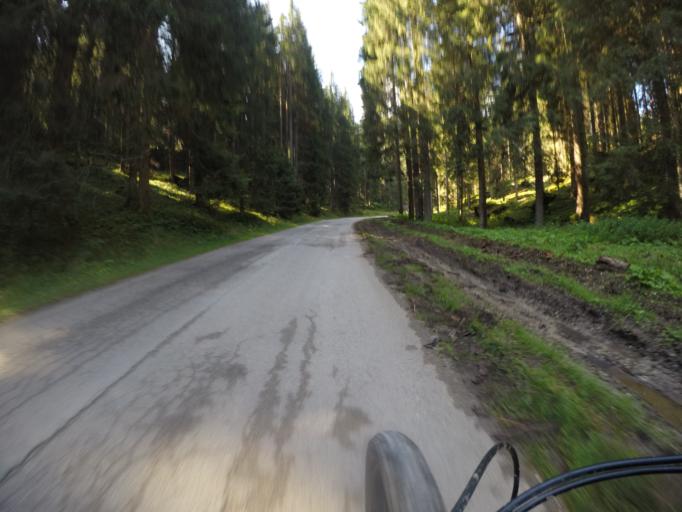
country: IT
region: Veneto
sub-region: Provincia di Vicenza
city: Asiago
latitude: 45.8368
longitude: 11.5213
